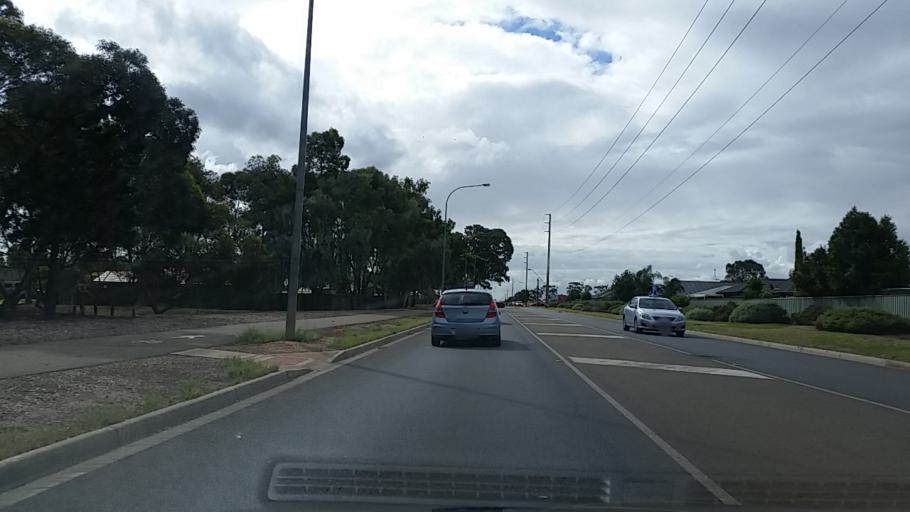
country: AU
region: South Australia
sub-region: Playford
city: Smithfield
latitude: -34.6656
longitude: 138.6646
